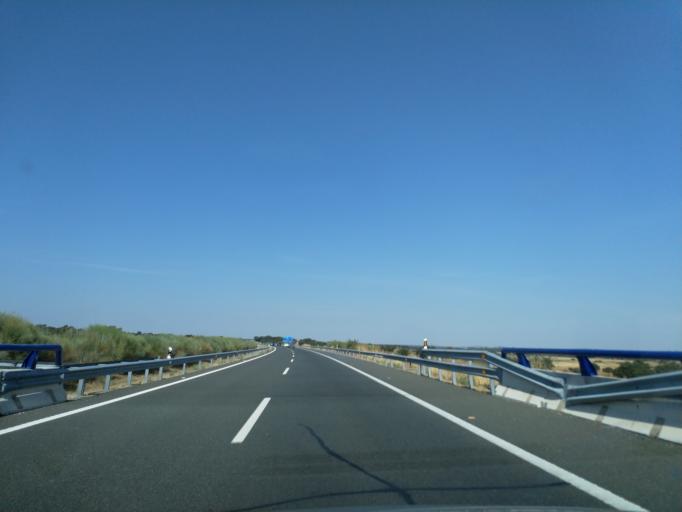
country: ES
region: Extremadura
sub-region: Provincia de Caceres
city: Casas de Don Antonio
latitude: 39.2165
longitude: -6.2900
